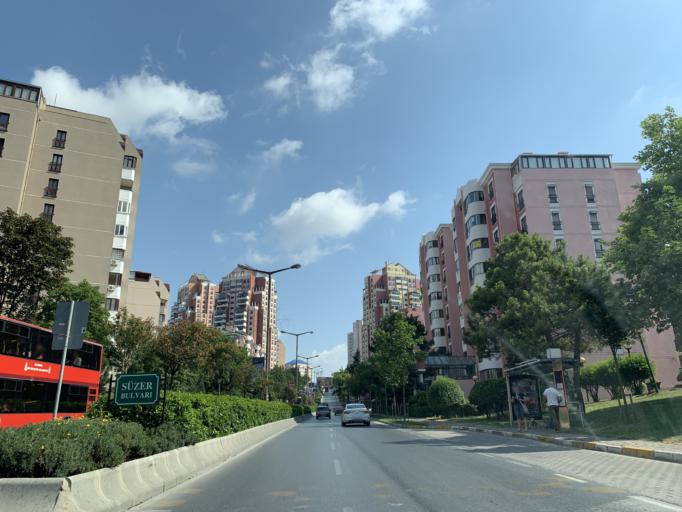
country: TR
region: Istanbul
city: Esenyurt
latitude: 41.0673
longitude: 28.6844
